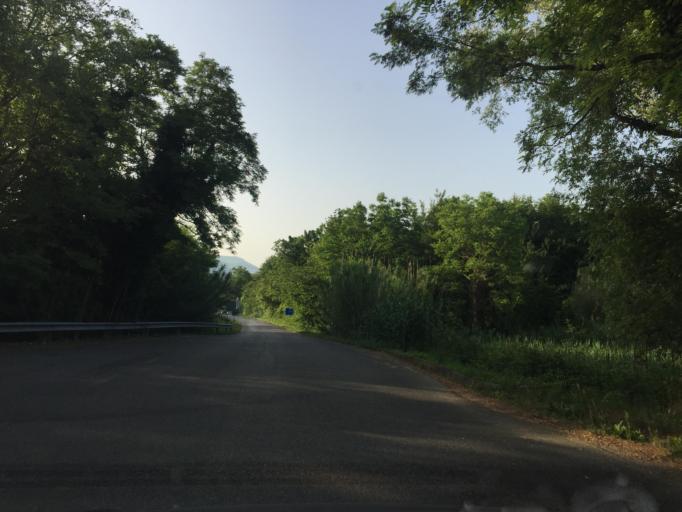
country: IT
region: Friuli Venezia Giulia
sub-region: Provincia di Trieste
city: Dolina
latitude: 45.5828
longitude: 13.8384
